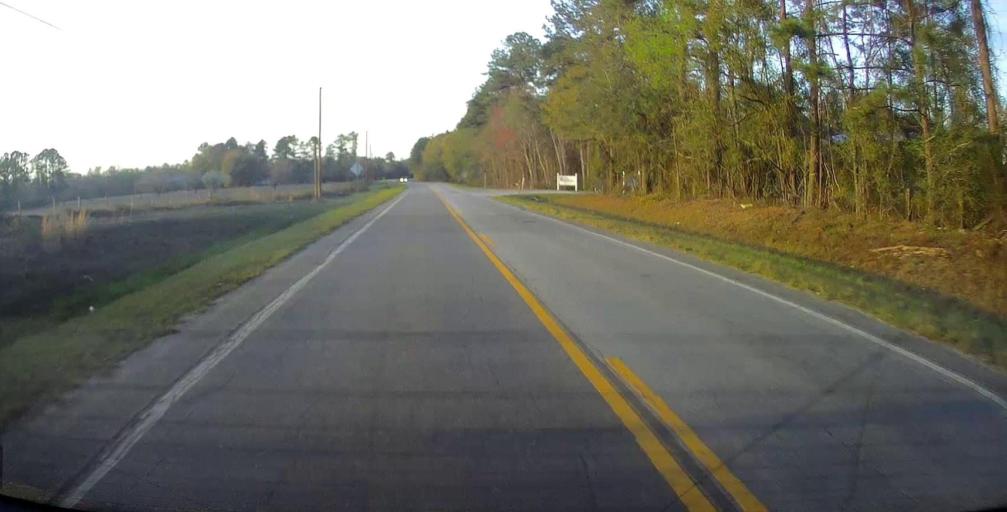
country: US
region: Georgia
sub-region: Chatham County
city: Bloomingdale
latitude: 32.1386
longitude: -81.3897
